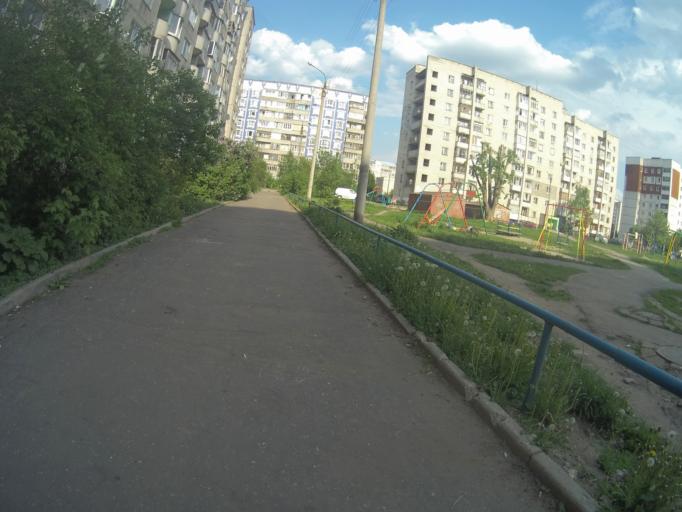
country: RU
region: Vladimir
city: Kommunar
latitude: 56.1694
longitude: 40.4465
